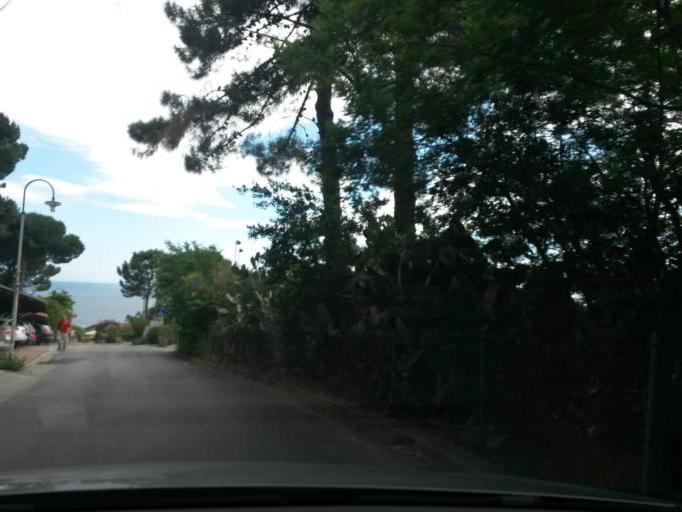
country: IT
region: Tuscany
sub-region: Provincia di Livorno
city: Marciana
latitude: 42.8031
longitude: 10.1385
